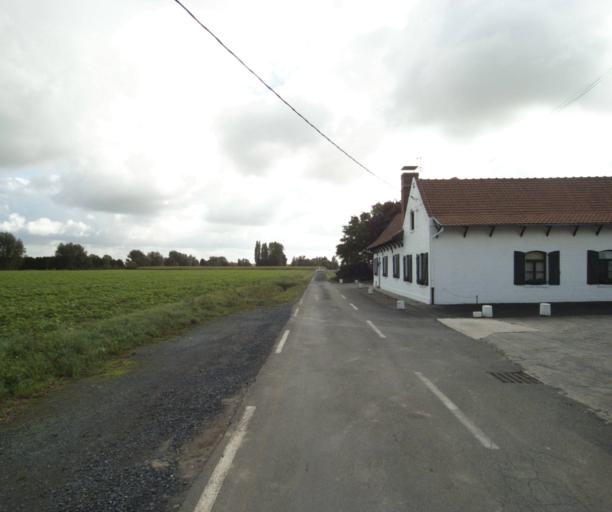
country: FR
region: Nord-Pas-de-Calais
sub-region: Departement du Nord
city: Houplines
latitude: 50.6797
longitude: 2.9257
